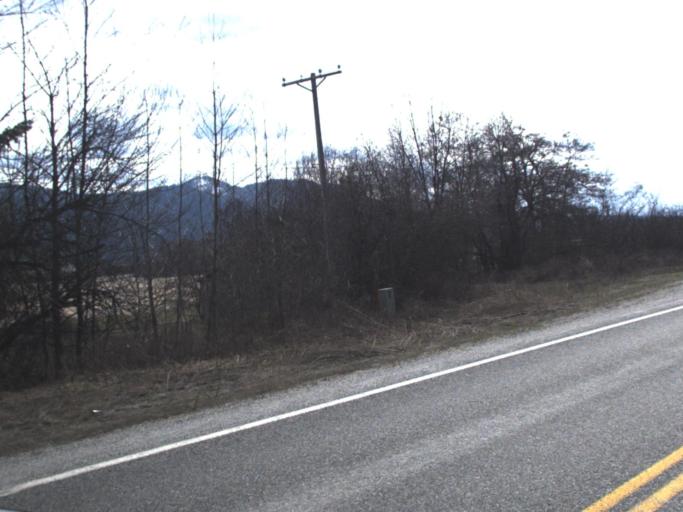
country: US
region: Washington
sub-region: Pend Oreille County
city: Newport
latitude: 48.4106
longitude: -117.3130
